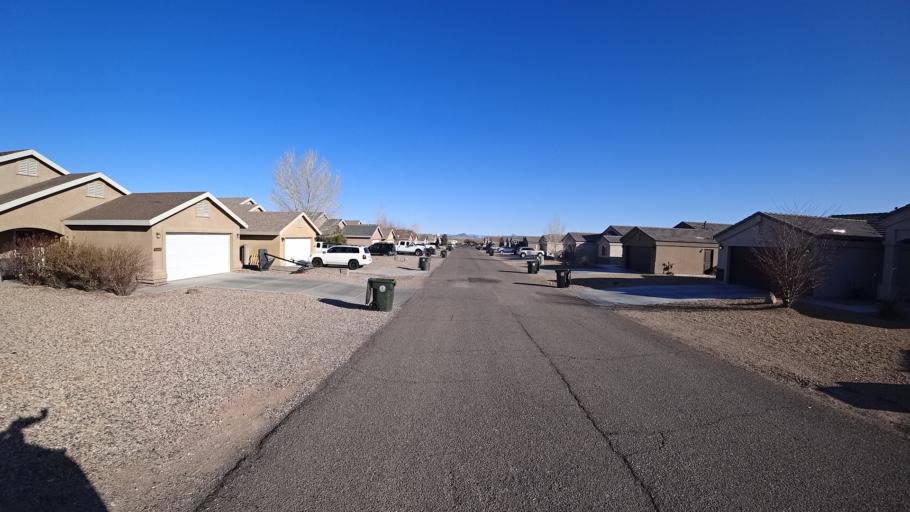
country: US
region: Arizona
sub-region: Mohave County
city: Kingman
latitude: 35.2108
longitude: -114.0060
